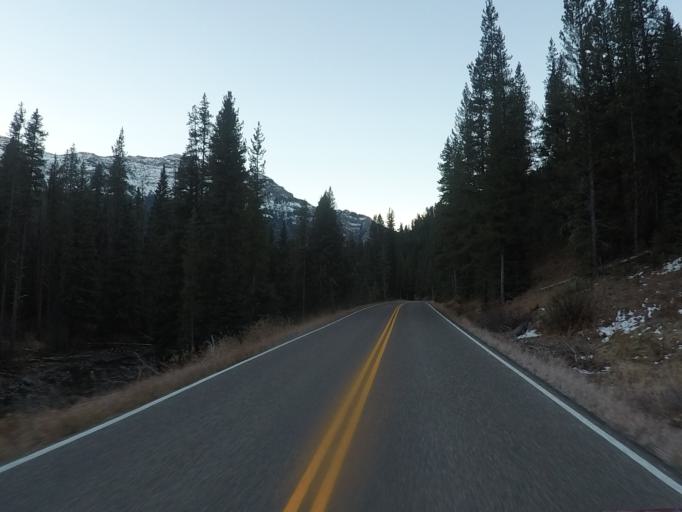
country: US
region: Montana
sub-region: Stillwater County
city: Absarokee
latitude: 44.9435
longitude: -110.0832
